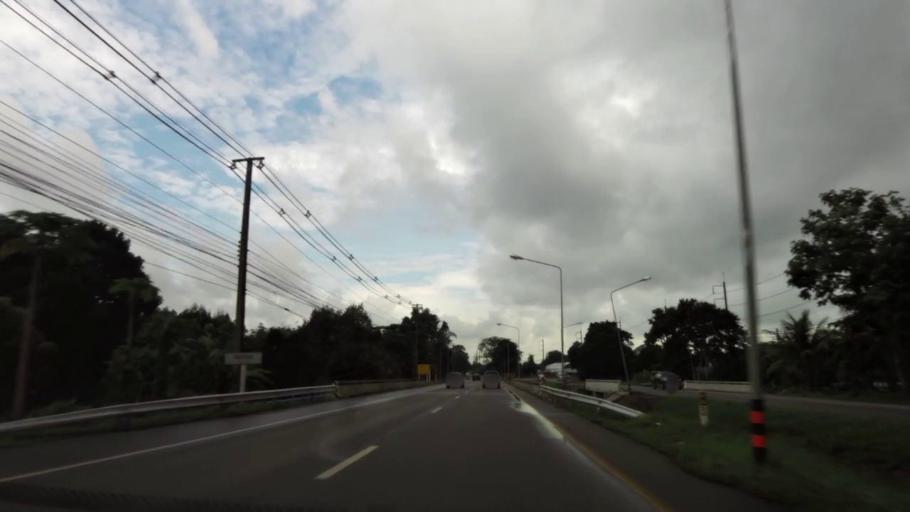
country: TH
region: Chanthaburi
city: Khlung
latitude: 12.4820
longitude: 102.1821
